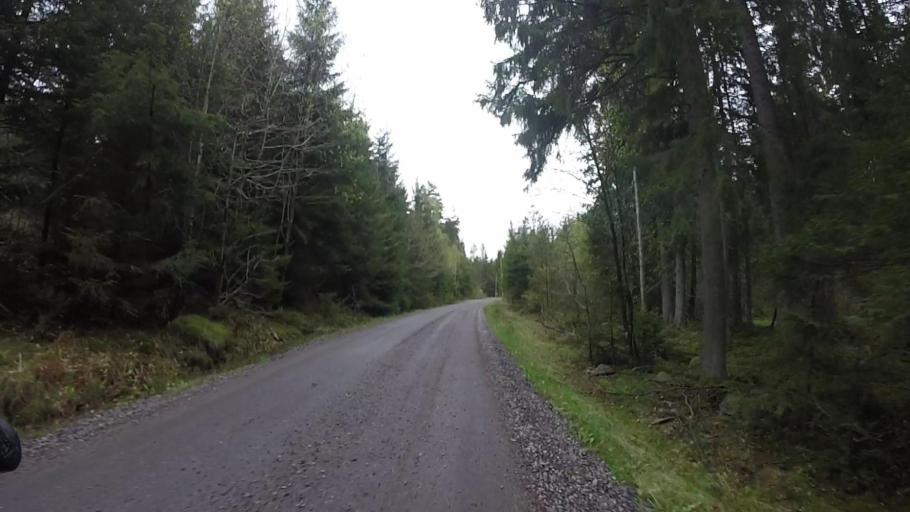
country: SE
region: Vaestra Goetaland
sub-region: Trollhattan
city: Sjuntorp
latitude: 58.2106
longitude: 12.2119
